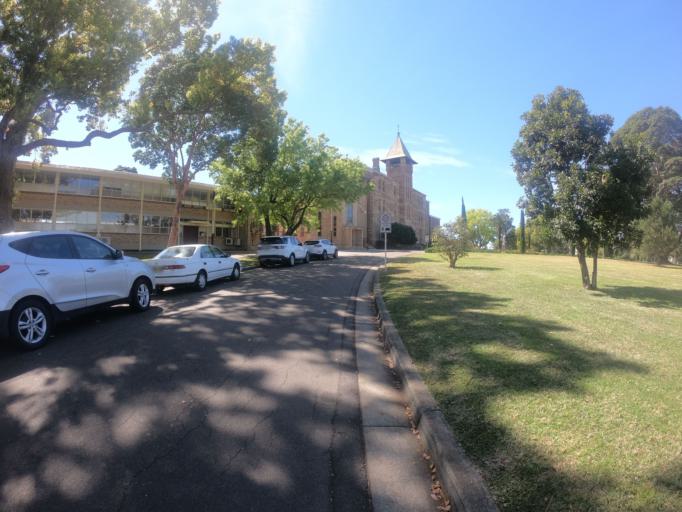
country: AU
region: New South Wales
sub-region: Ryde
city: East Ryde
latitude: -33.8194
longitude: 151.1179
